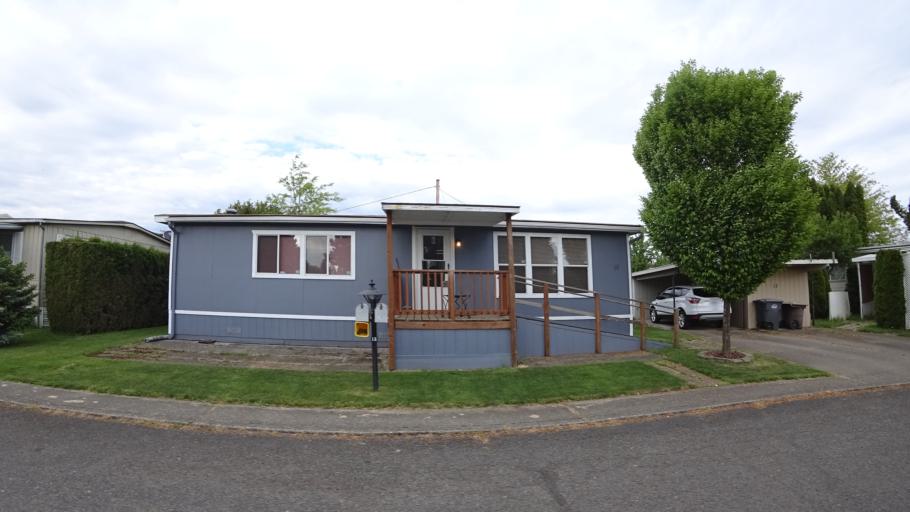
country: US
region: Oregon
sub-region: Washington County
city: Hillsboro
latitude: 45.5019
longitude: -122.9533
